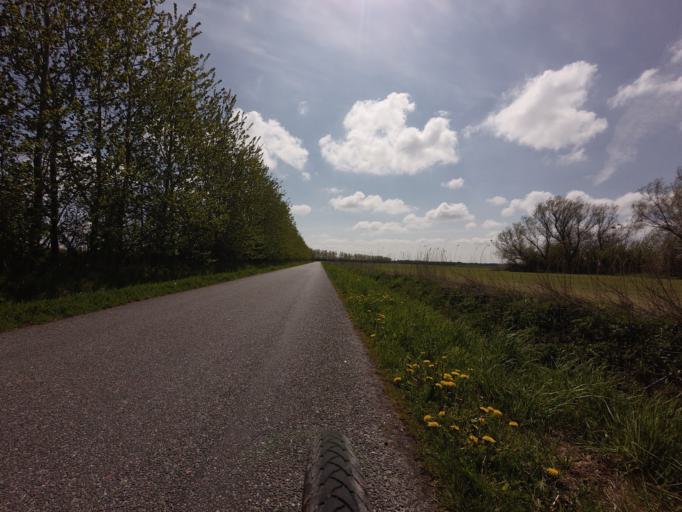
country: DK
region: North Denmark
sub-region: Jammerbugt Kommune
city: Brovst
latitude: 57.1407
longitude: 9.5229
